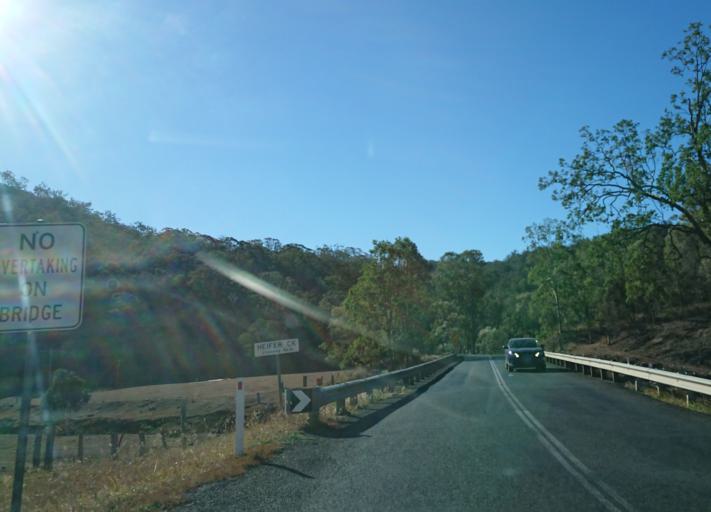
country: AU
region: Queensland
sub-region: Toowoomba
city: Top Camp
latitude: -27.7546
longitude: 152.0814
